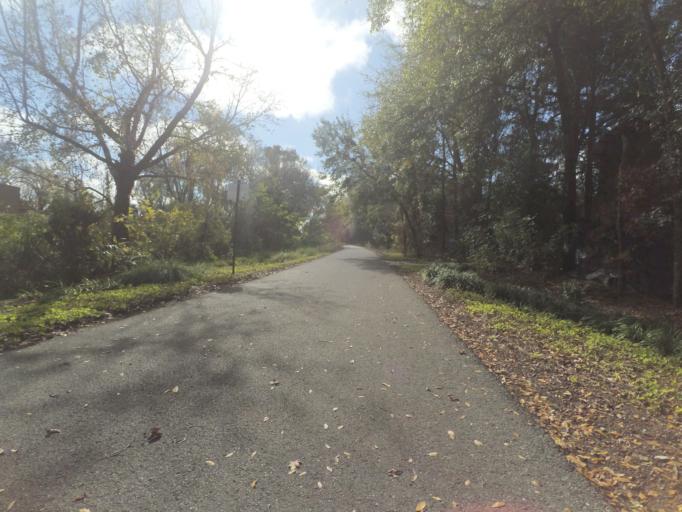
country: US
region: Florida
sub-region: Alachua County
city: Gainesville
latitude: 29.6664
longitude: -82.3259
